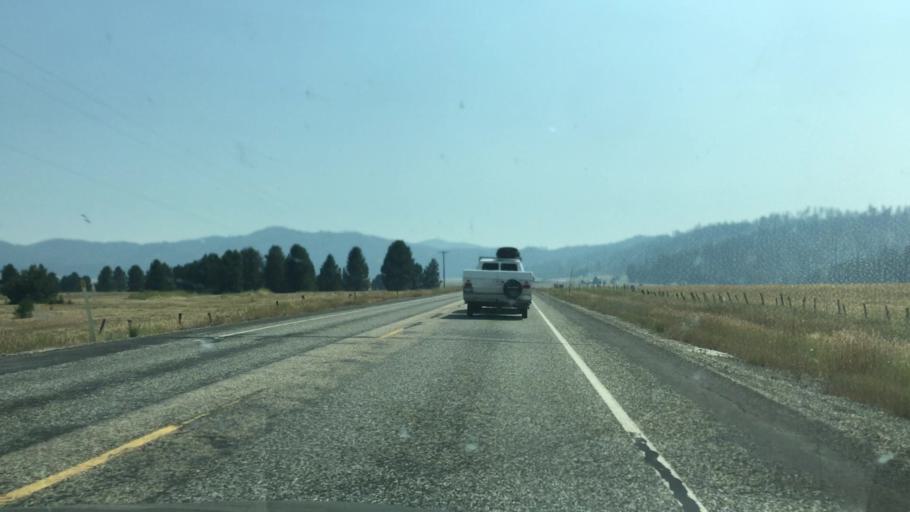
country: US
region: Idaho
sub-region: Valley County
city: Cascade
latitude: 44.3447
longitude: -116.0276
